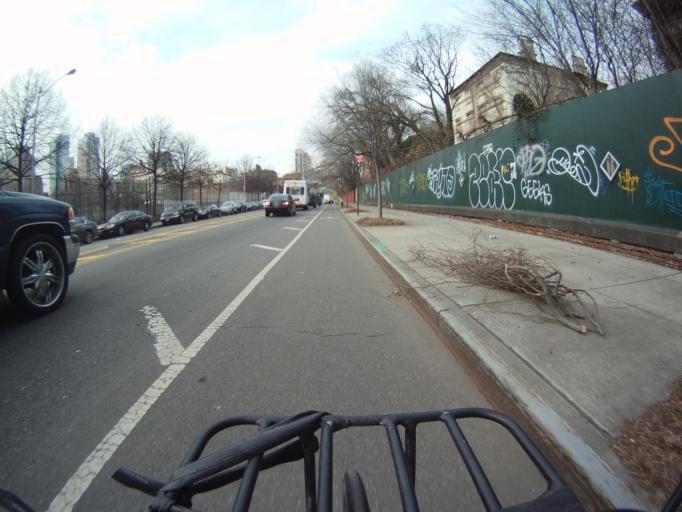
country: US
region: New York
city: New York City
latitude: 40.6982
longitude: -73.9789
